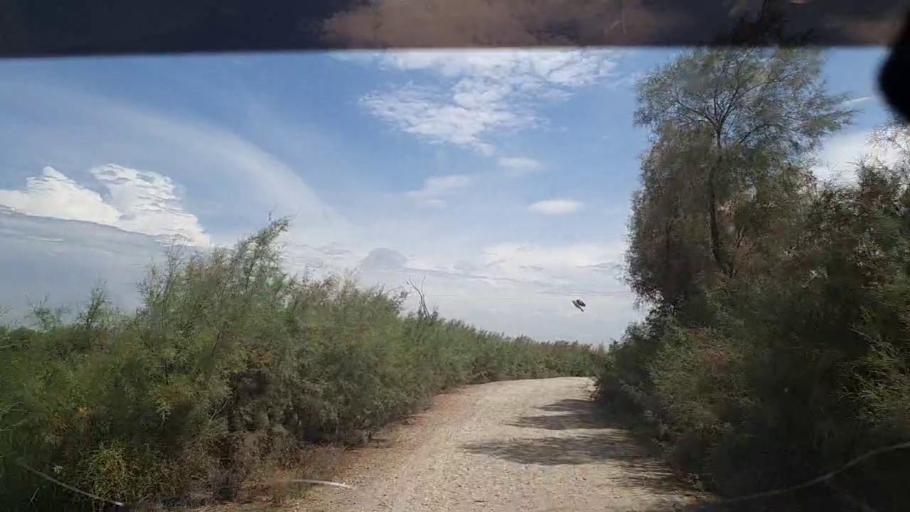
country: PK
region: Sindh
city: Ghauspur
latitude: 28.1447
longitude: 68.9779
